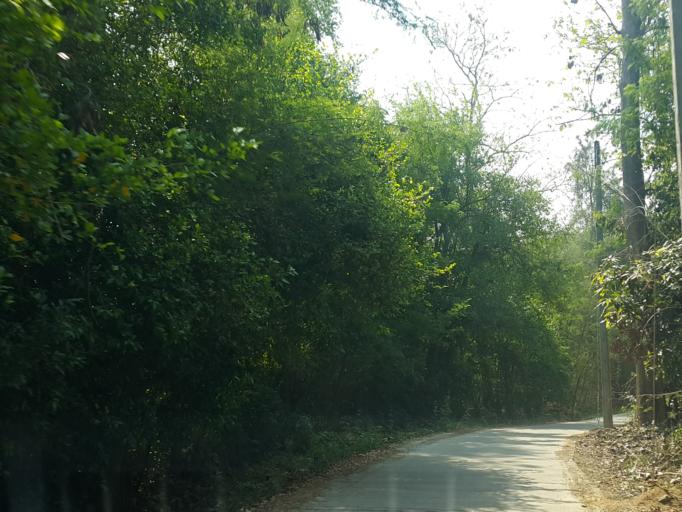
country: TH
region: Chiang Mai
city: San Kamphaeng
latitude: 18.7558
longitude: 99.1385
